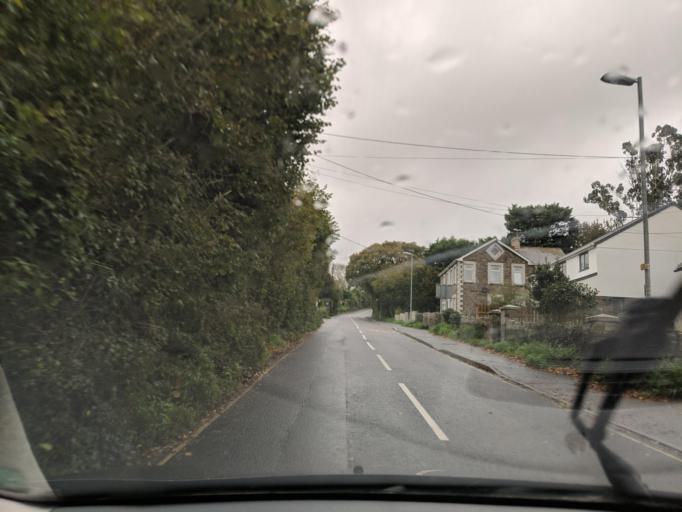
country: GB
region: England
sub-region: Cornwall
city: Bodmin
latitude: 50.4642
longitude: -4.7186
